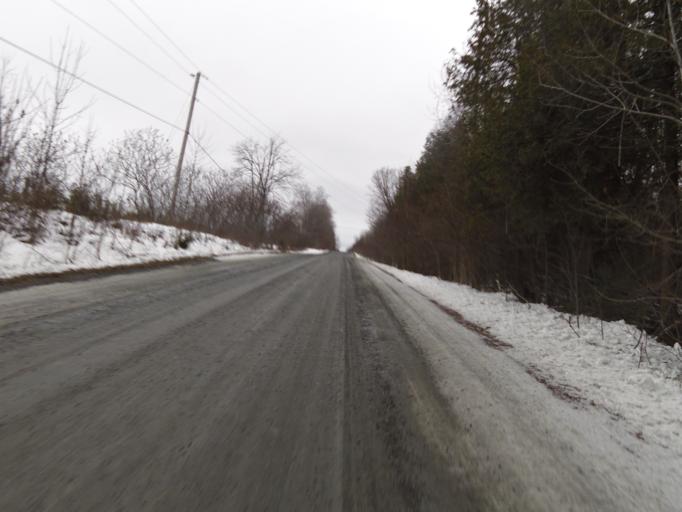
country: CA
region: Ontario
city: Carleton Place
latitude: 45.1109
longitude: -76.2527
